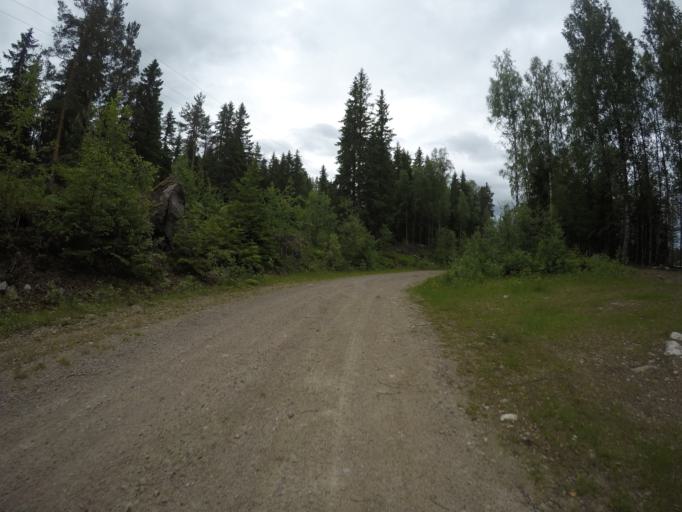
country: SE
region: Dalarna
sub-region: Ludvika Kommun
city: Abborrberget
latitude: 60.0726
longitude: 14.5647
